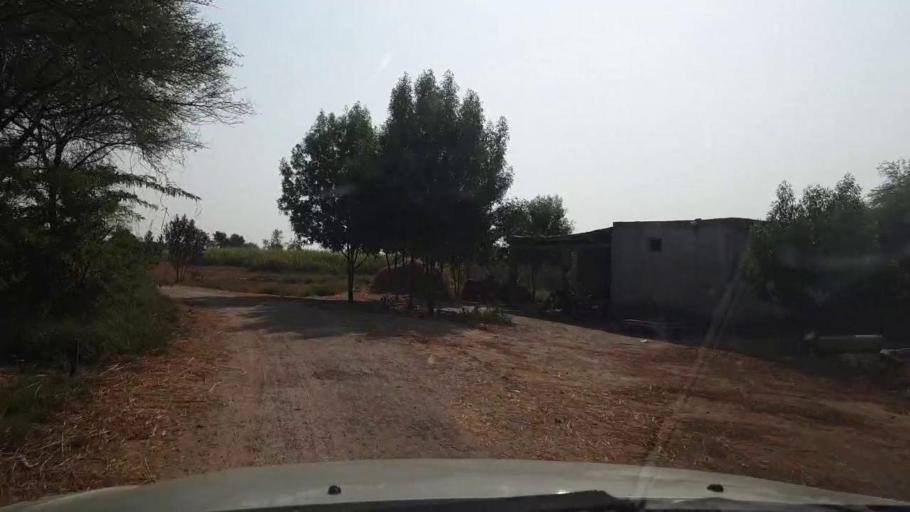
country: PK
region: Sindh
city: Bulri
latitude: 24.9039
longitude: 68.3758
